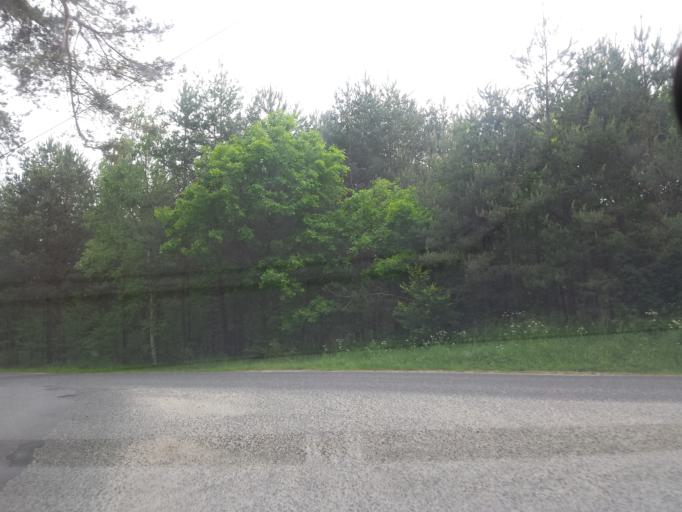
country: CZ
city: Cvikov
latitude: 50.7452
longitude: 14.6029
